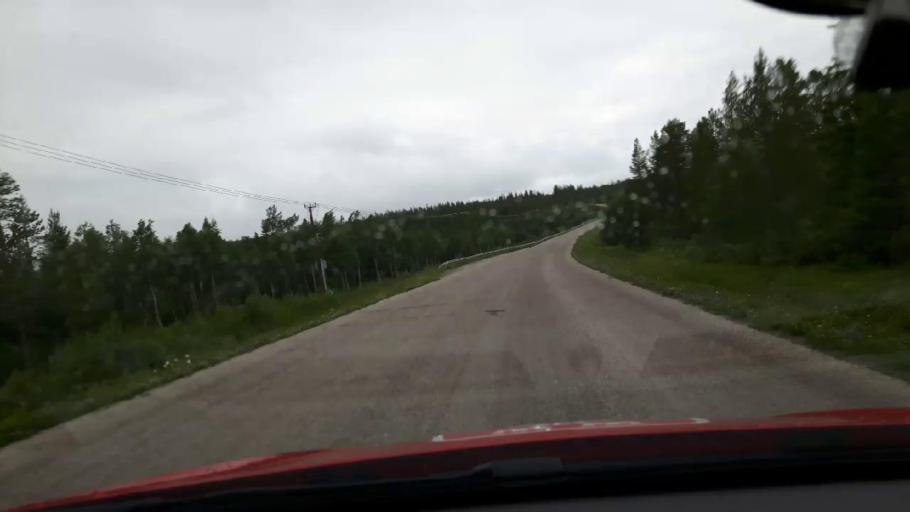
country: NO
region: Nord-Trondelag
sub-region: Meraker
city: Meraker
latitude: 63.2795
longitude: 12.3543
